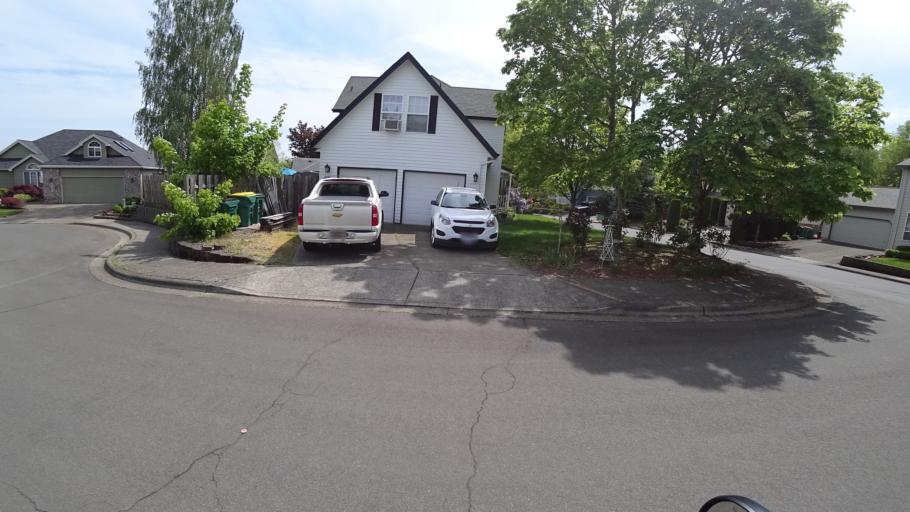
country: US
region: Oregon
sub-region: Washington County
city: Aloha
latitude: 45.4597
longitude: -122.8488
